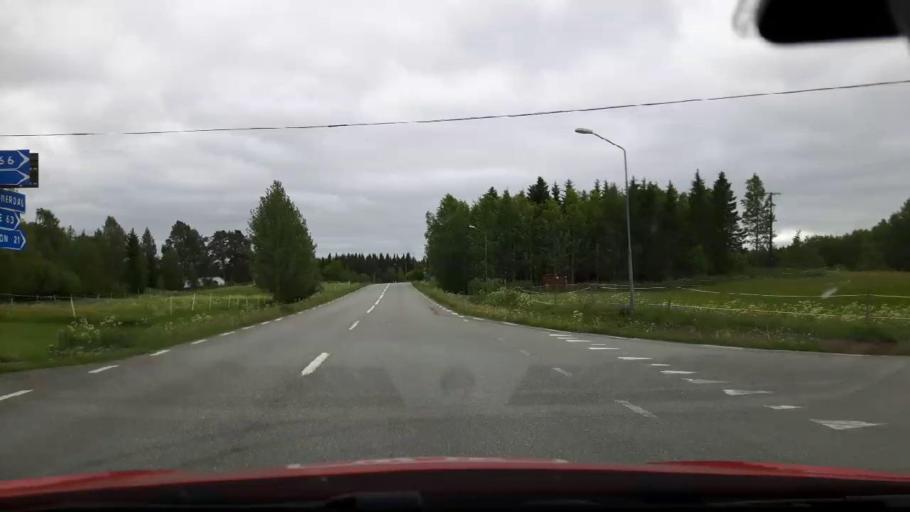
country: SE
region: Jaemtland
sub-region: Stroemsunds Kommun
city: Stroemsund
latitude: 63.5507
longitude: 15.4050
